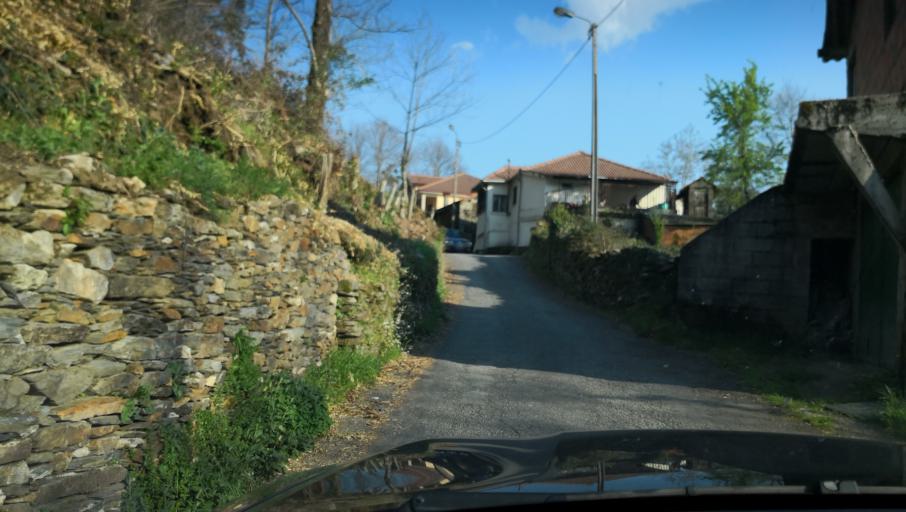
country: PT
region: Vila Real
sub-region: Vila Real
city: Vila Real
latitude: 41.3150
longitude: -7.8543
